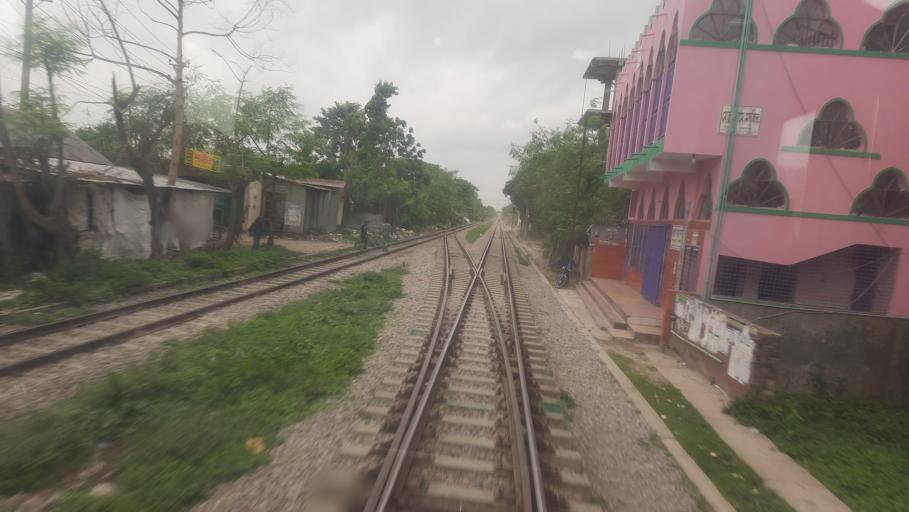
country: BD
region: Dhaka
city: Narsingdi
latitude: 23.9310
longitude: 90.7138
